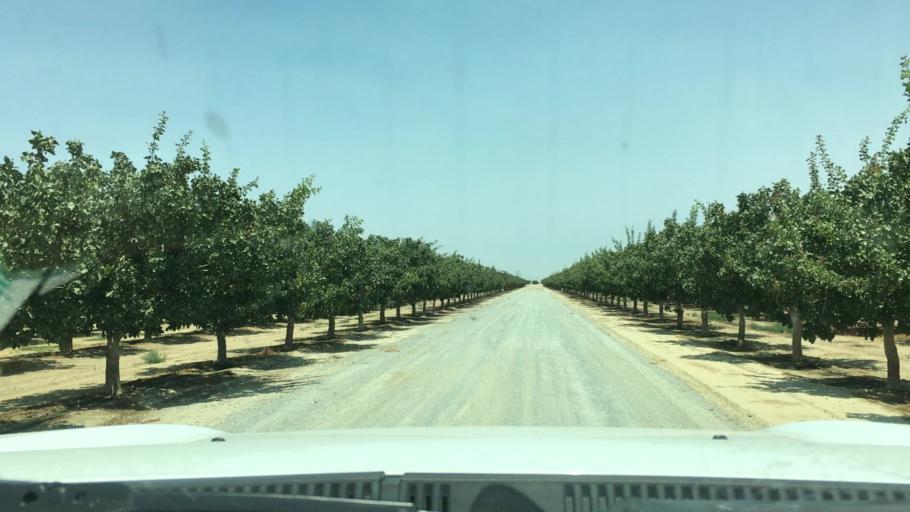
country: US
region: California
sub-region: Kern County
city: Wasco
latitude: 35.6757
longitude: -119.4286
